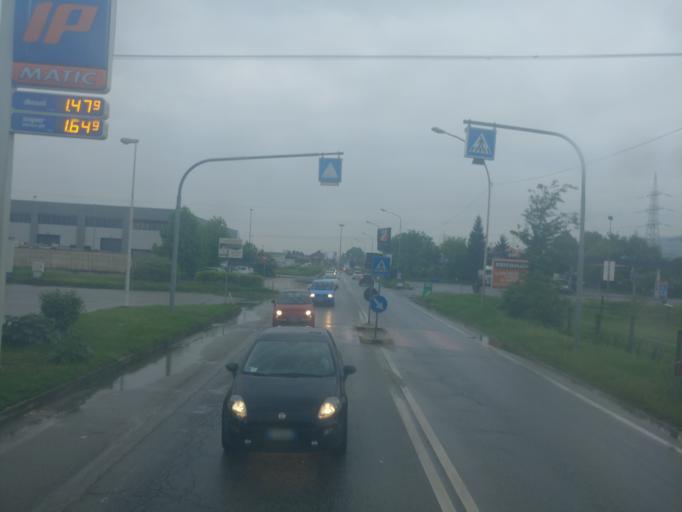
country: IT
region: Piedmont
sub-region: Provincia di Torino
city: Tagliaferro
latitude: 44.9821
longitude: 7.6707
